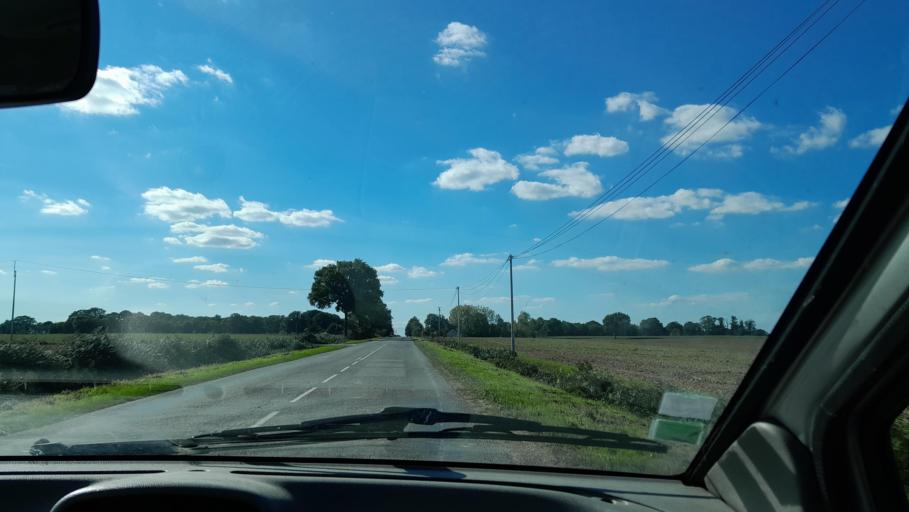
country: FR
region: Brittany
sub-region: Departement d'Ille-et-Vilaine
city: Le Pertre
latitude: 47.9682
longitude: -1.0814
